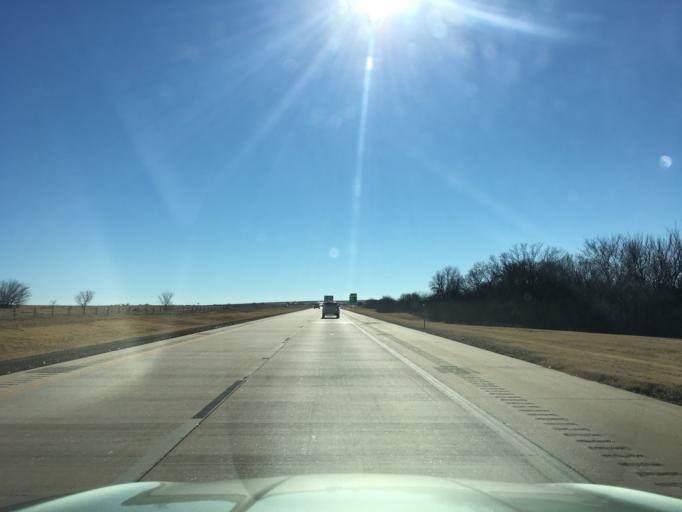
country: US
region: Oklahoma
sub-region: Noble County
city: Perry
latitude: 36.4215
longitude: -97.3271
